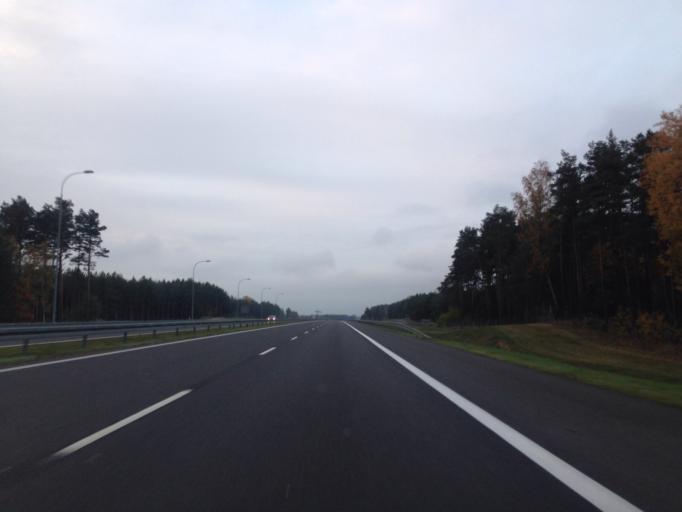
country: PL
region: Kujawsko-Pomorskie
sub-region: Powiat swiecki
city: Warlubie
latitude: 53.6270
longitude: 18.6383
